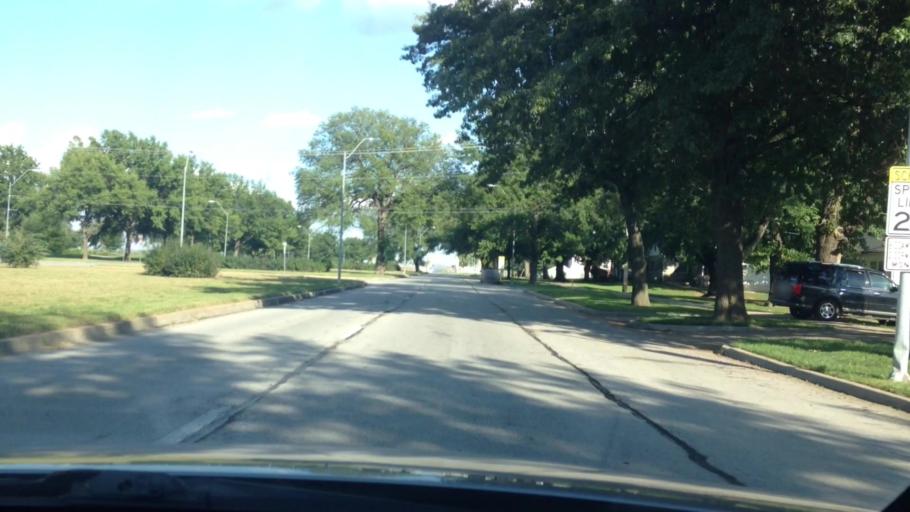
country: US
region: Kansas
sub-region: Johnson County
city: Mission Hills
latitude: 39.0075
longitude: -94.5480
